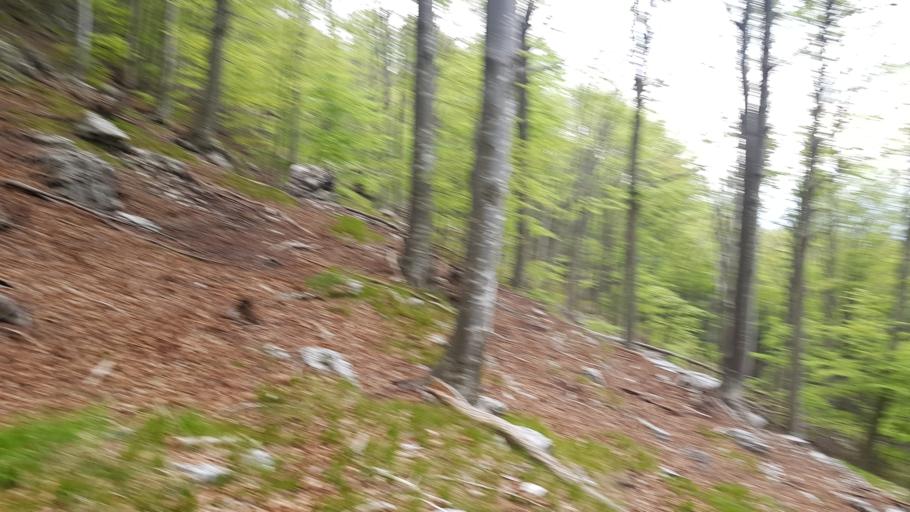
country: IT
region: Friuli Venezia Giulia
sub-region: Provincia di Udine
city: Chiaulis
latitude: 46.3122
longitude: 12.9756
